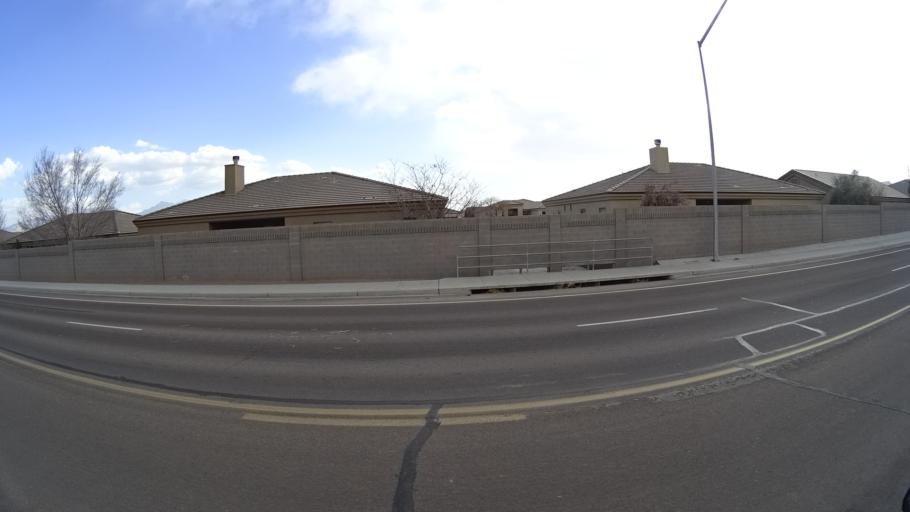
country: US
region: Arizona
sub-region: Mohave County
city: New Kingman-Butler
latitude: 35.2395
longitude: -114.0309
